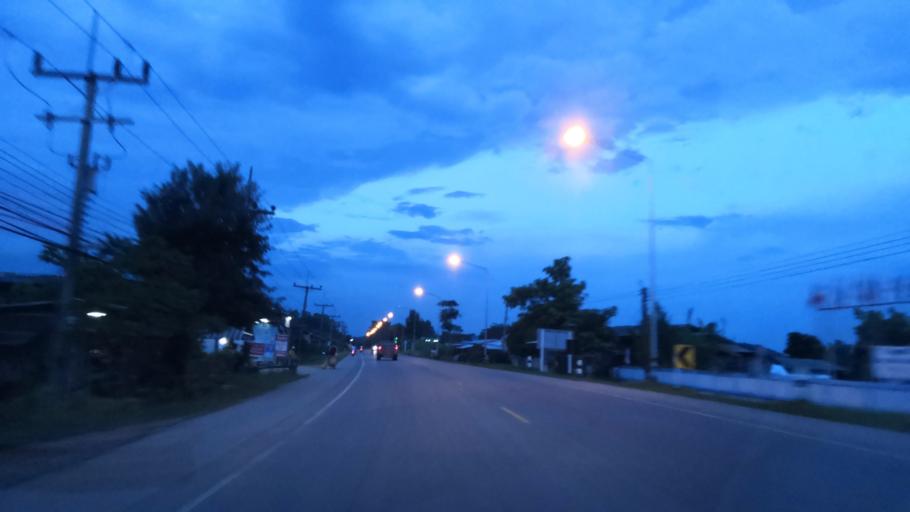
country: TH
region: Chiang Rai
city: Wiang Chiang Rung
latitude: 19.9791
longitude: 100.0231
